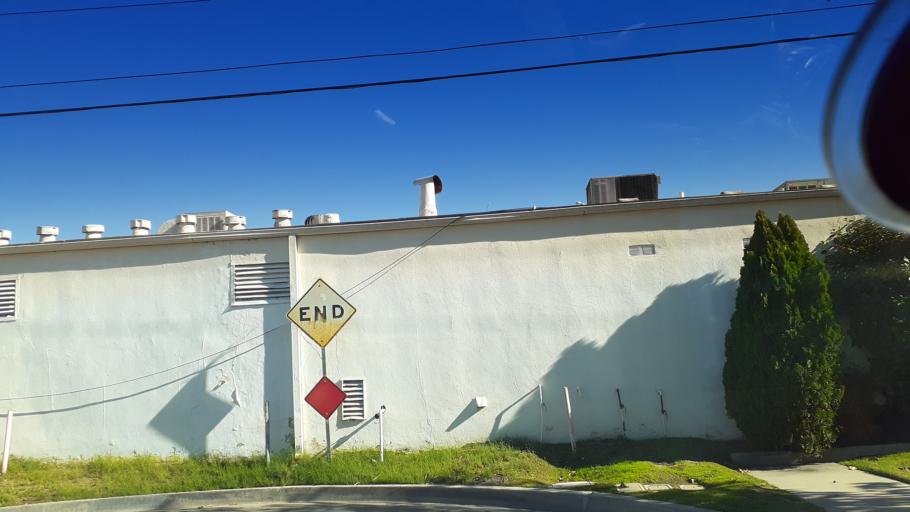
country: US
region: California
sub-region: Los Angeles County
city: Cerritos
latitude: 33.8590
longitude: -118.0736
